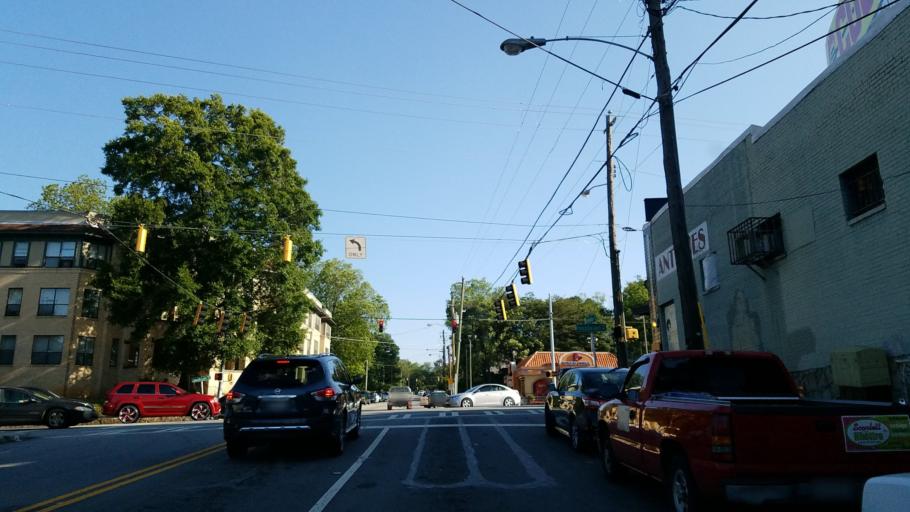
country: US
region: Georgia
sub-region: Fulton County
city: Atlanta
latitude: 33.7735
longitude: -84.3728
